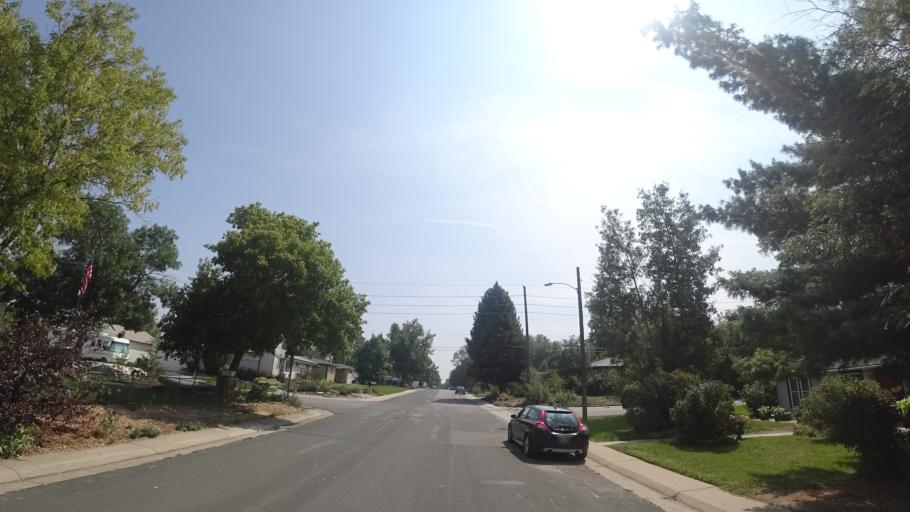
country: US
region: Colorado
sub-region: Arapahoe County
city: Englewood
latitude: 39.6298
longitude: -104.9961
